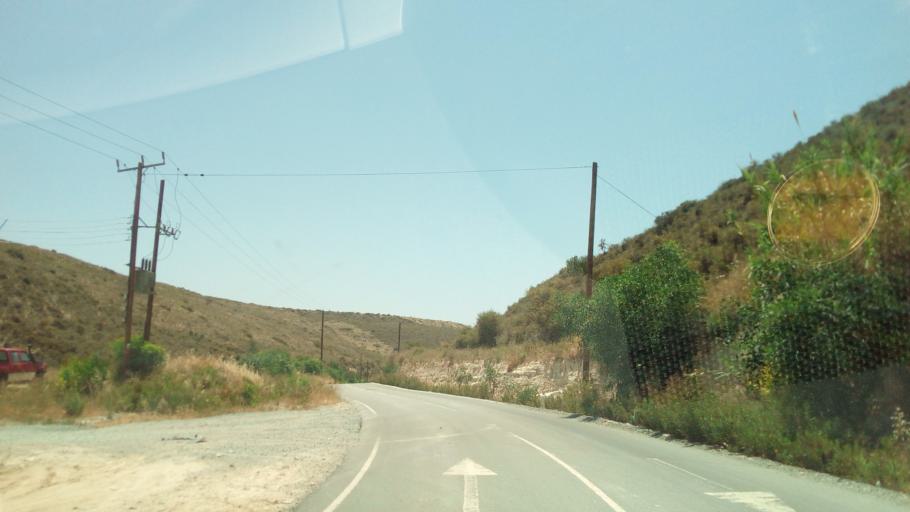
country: CY
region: Limassol
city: Ypsonas
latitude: 34.7407
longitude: 32.9447
